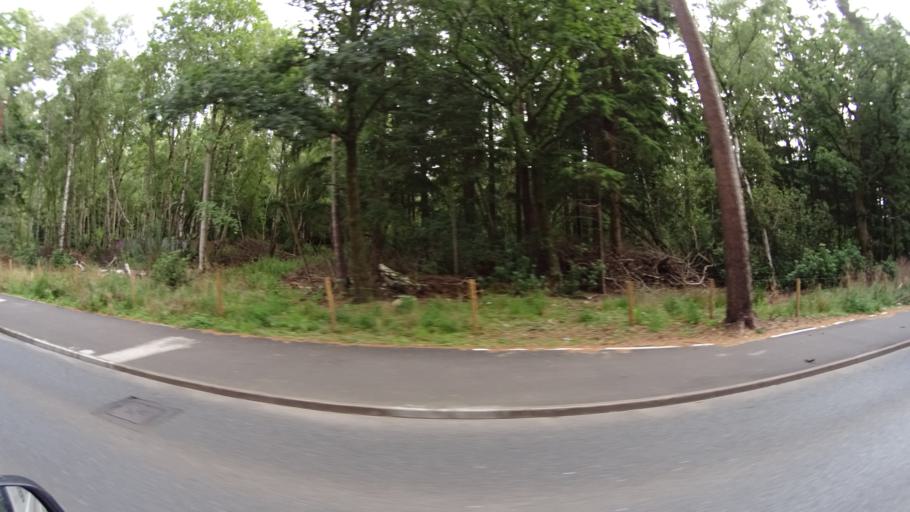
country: GB
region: England
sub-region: Dorset
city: Christchurch
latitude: 50.7669
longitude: -1.8155
